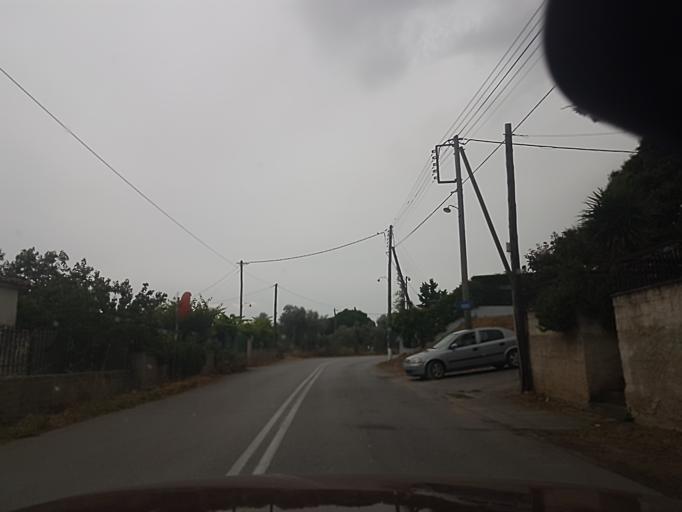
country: GR
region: Central Greece
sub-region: Nomos Evvoias
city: Mytikas
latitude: 38.4649
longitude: 23.6319
